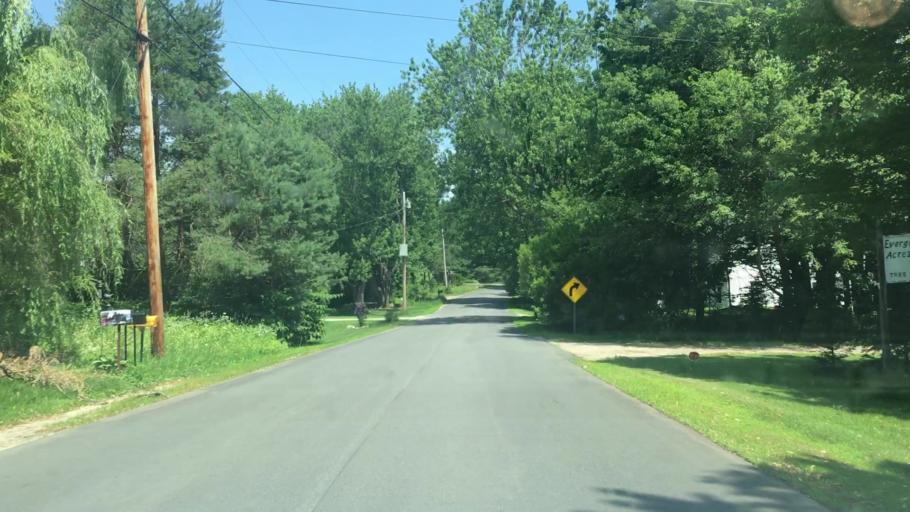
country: US
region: Maine
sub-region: Kennebec County
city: Monmouth
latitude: 44.2707
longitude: -70.0519
